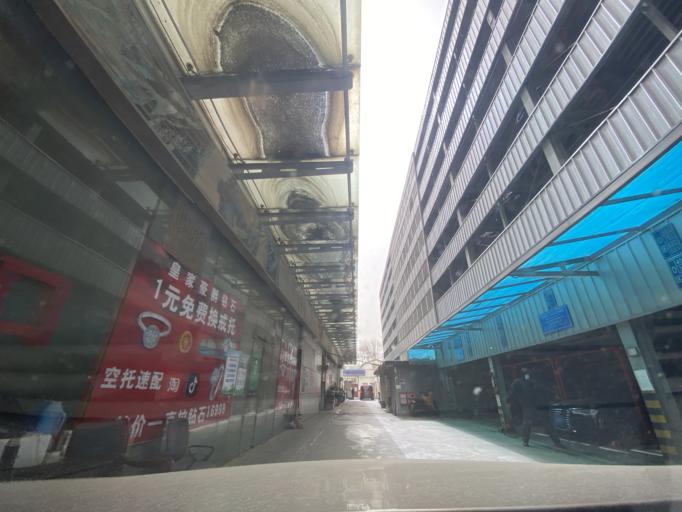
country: CN
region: Beijing
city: Jinrongjie
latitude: 39.9415
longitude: 116.3653
